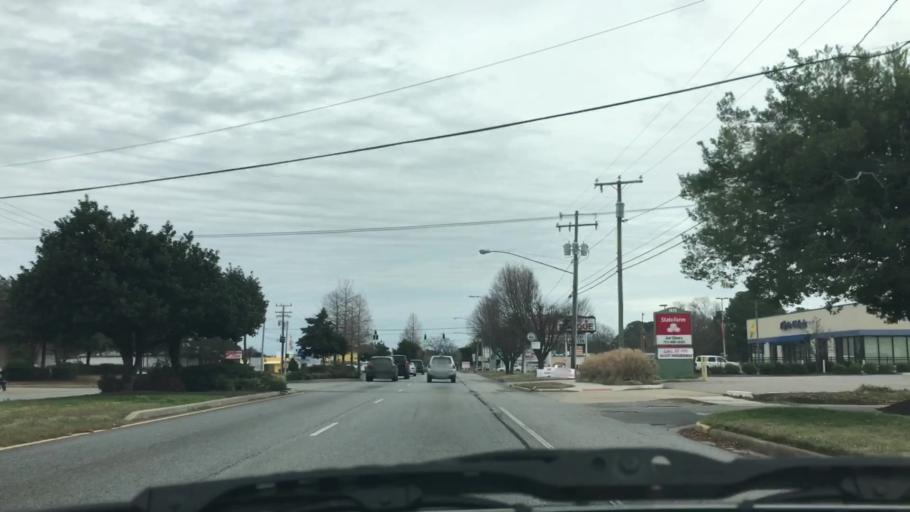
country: US
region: Virginia
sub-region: City of Norfolk
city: Norfolk
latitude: 36.9162
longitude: -76.2264
